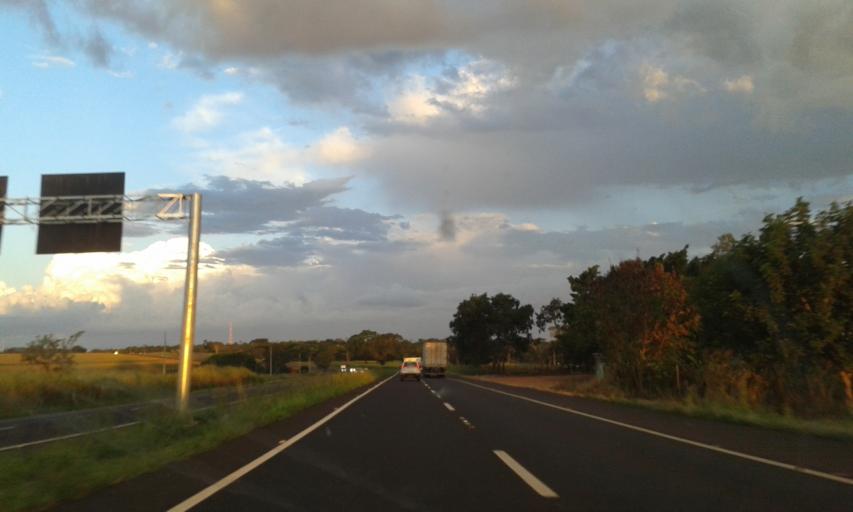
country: BR
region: Minas Gerais
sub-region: Monte Alegre De Minas
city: Monte Alegre de Minas
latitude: -18.8812
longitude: -48.7407
